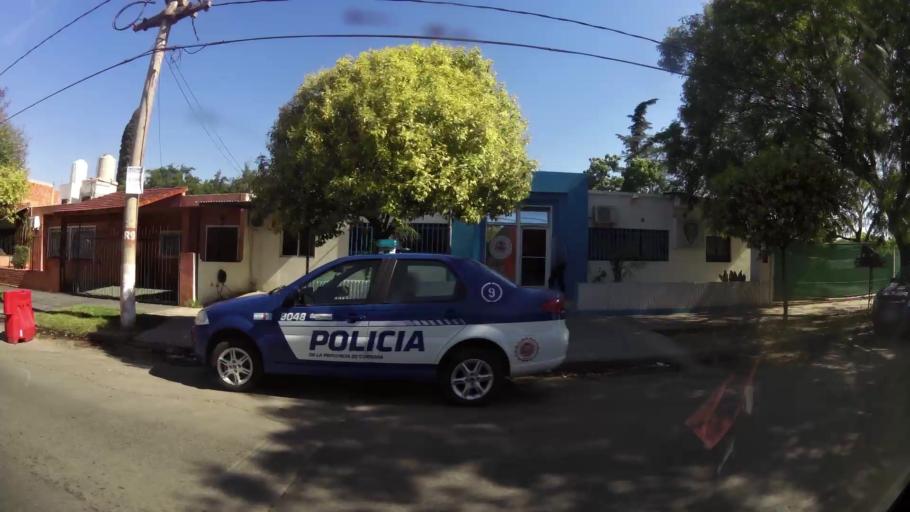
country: AR
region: Cordoba
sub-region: Departamento de Capital
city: Cordoba
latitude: -31.3700
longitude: -64.1813
